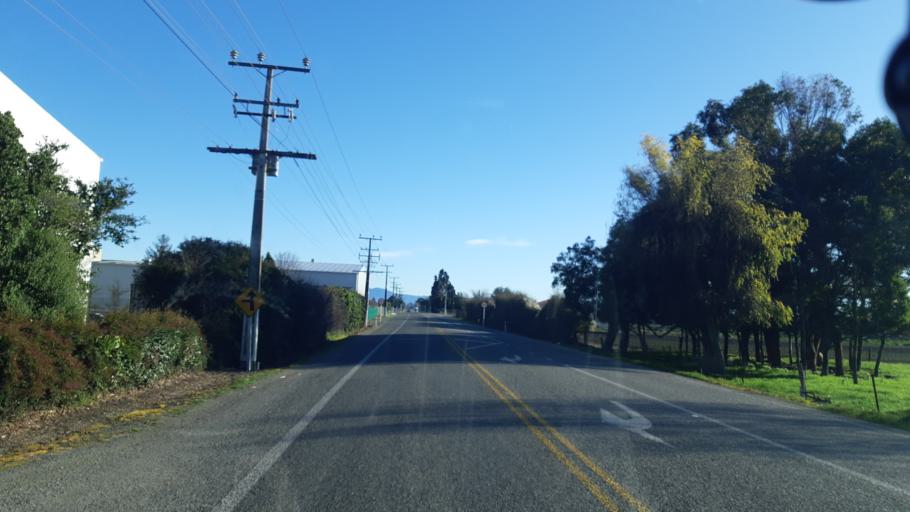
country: NZ
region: Tasman
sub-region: Tasman District
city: Richmond
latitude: -41.3199
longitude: 173.1397
